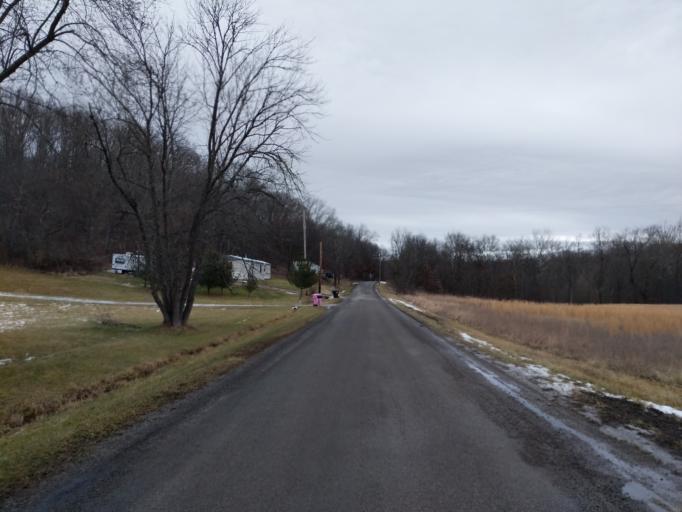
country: US
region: Ohio
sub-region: Athens County
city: The Plains
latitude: 39.3361
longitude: -82.1835
